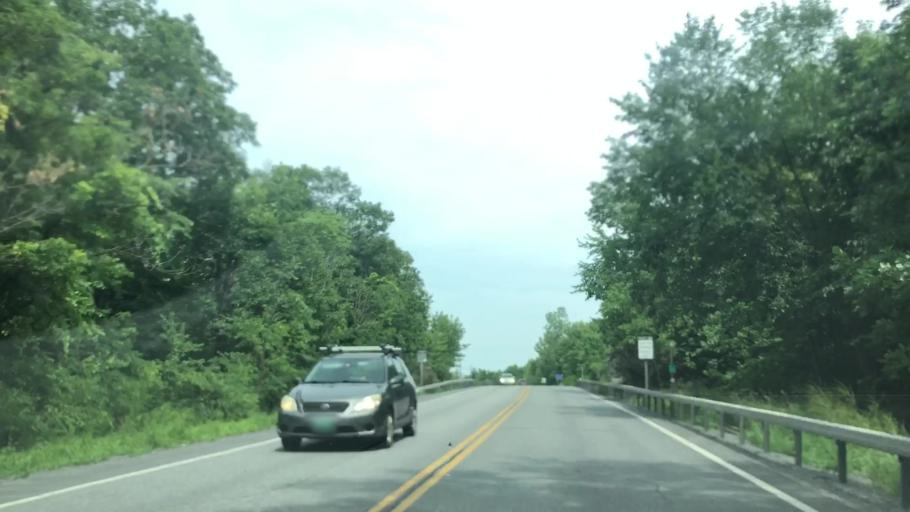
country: US
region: New York
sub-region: Washington County
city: Whitehall
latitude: 43.4293
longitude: -73.4688
